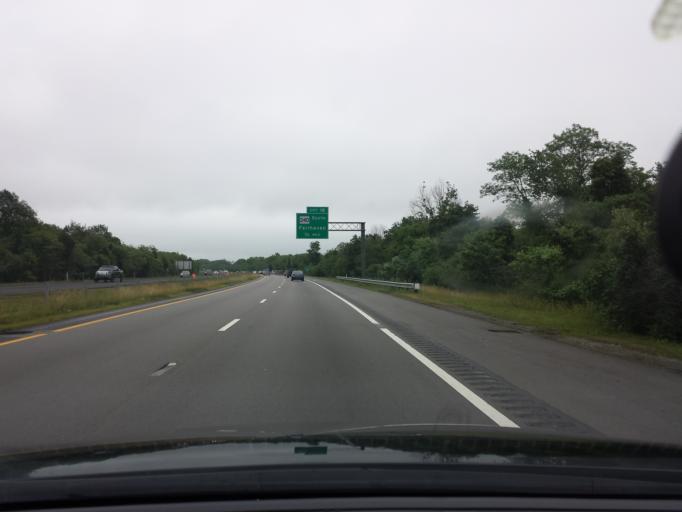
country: US
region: Massachusetts
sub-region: Bristol County
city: Fairhaven
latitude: 41.6541
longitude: -70.9054
